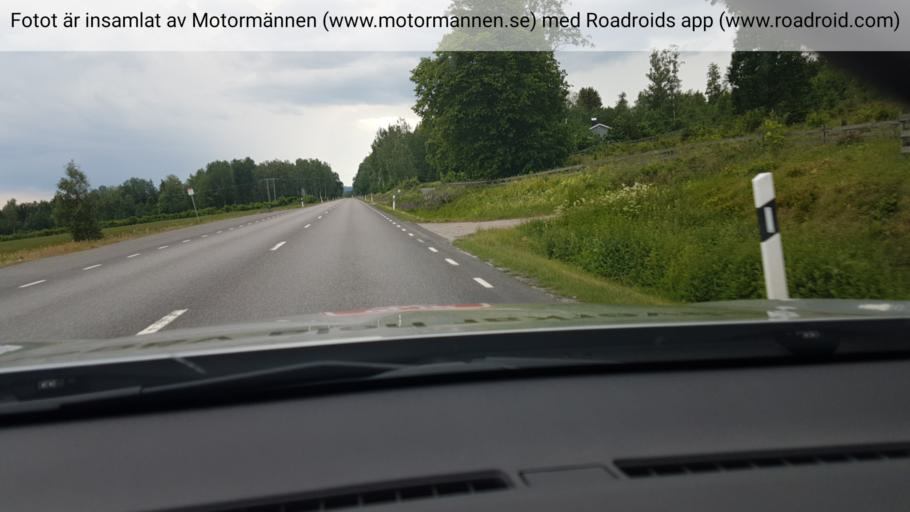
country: SE
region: Joenkoeping
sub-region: Habo Kommun
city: Habo
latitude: 57.9527
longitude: 14.1046
